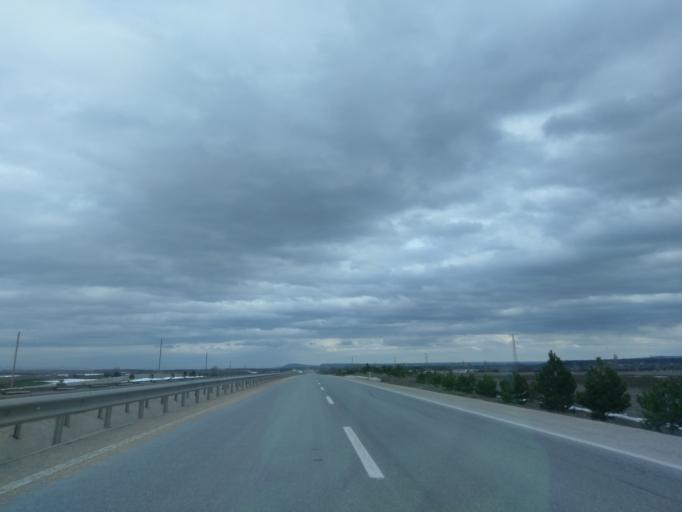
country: TR
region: Eskisehir
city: Inonu
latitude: 39.7245
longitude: 30.2790
